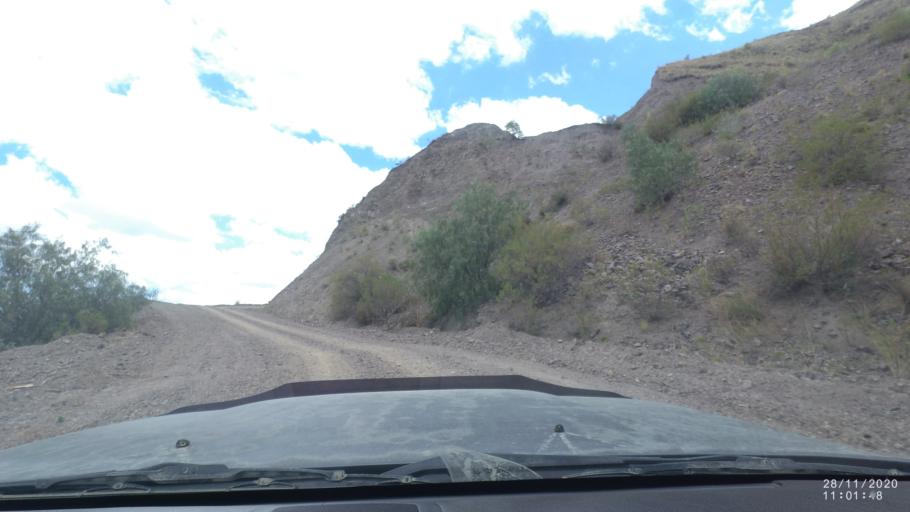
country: BO
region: Cochabamba
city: Capinota
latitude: -17.7658
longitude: -66.1050
